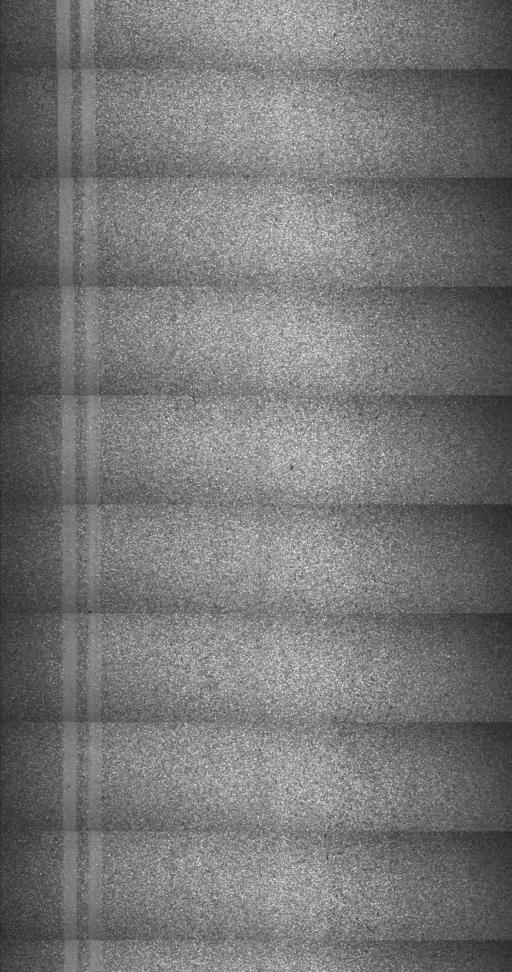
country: US
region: New York
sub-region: Clinton County
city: Rouses Point
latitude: 44.9541
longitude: -73.2711
